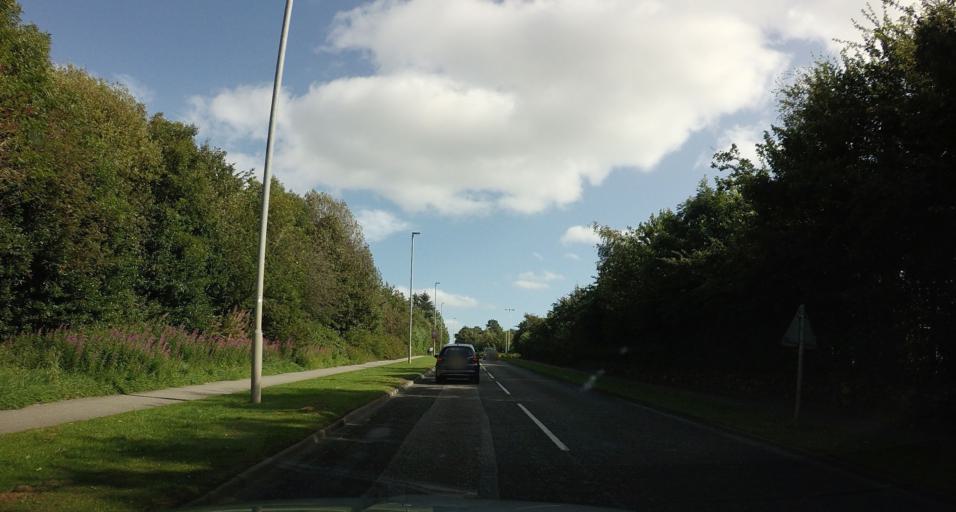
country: GB
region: Scotland
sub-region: Aberdeenshire
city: Westhill
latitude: 57.1515
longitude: -2.3044
